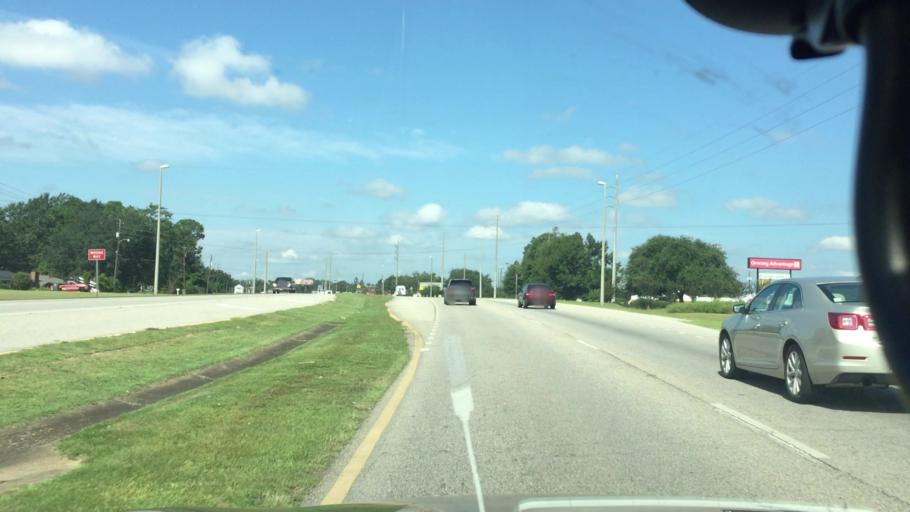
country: US
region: Alabama
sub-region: Coffee County
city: Enterprise
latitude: 31.3344
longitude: -85.8493
